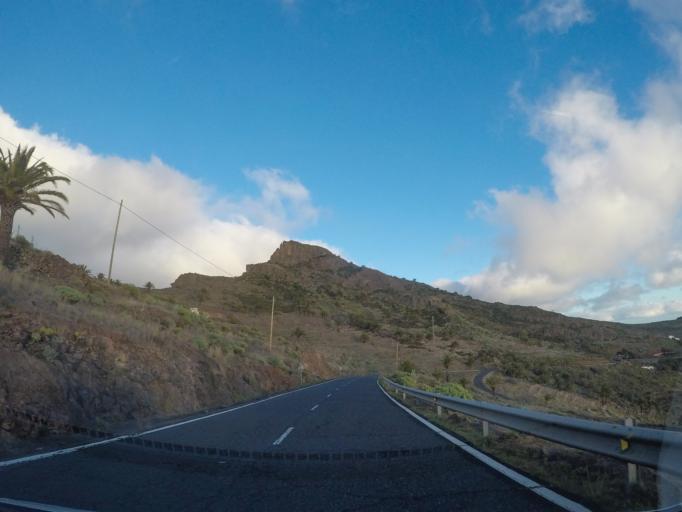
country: ES
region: Canary Islands
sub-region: Provincia de Santa Cruz de Tenerife
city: Alajero
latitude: 28.0758
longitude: -17.2411
